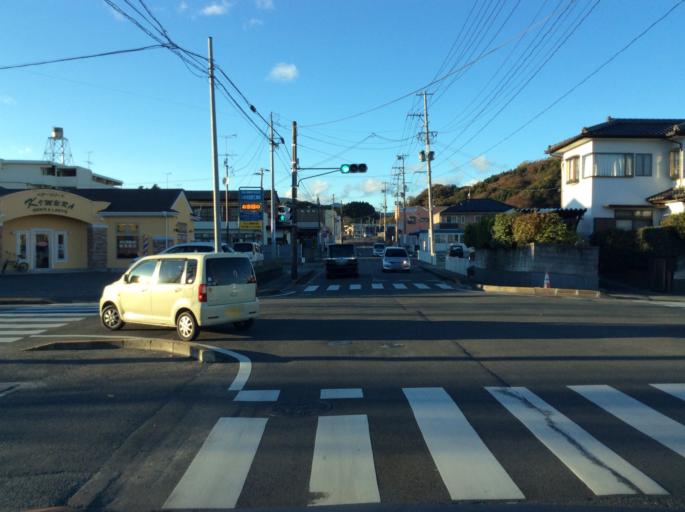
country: JP
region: Fukushima
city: Iwaki
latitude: 37.0503
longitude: 140.8735
